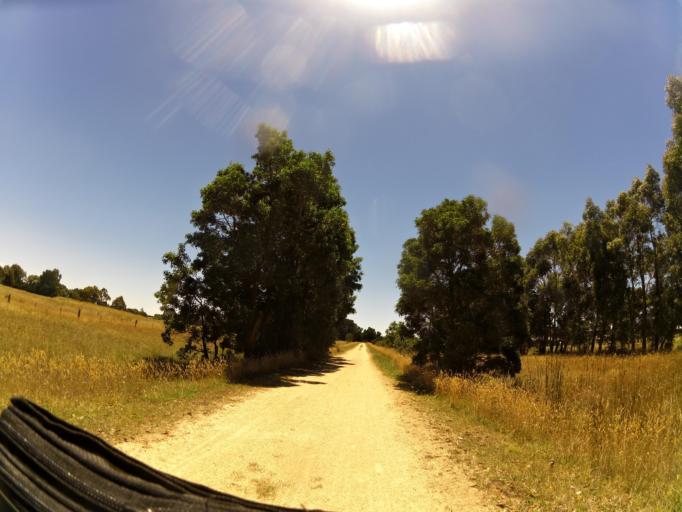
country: AU
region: Victoria
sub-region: Ballarat North
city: Delacombe
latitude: -37.5997
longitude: 143.7178
